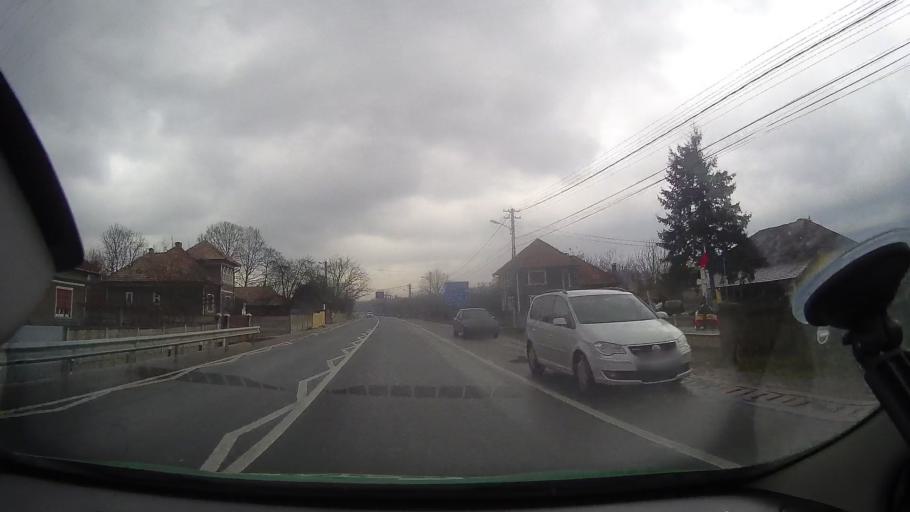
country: RO
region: Hunedoara
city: Vata de Jos
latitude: 46.1916
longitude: 22.6147
